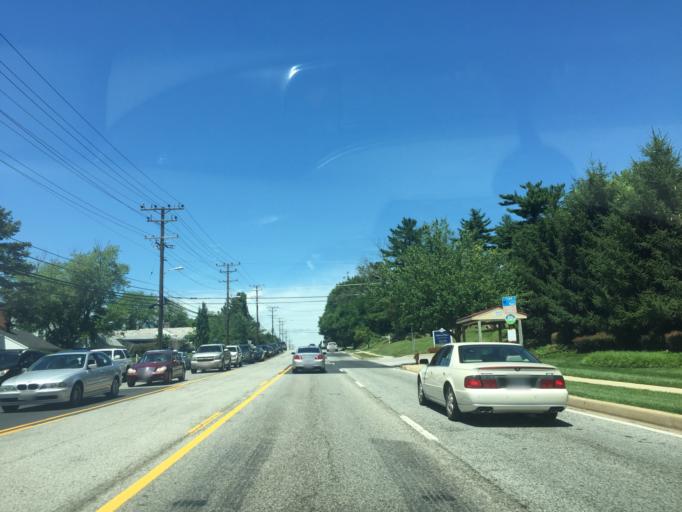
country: US
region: Maryland
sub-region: Baltimore County
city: Milford Mill
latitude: 39.3579
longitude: -76.7694
